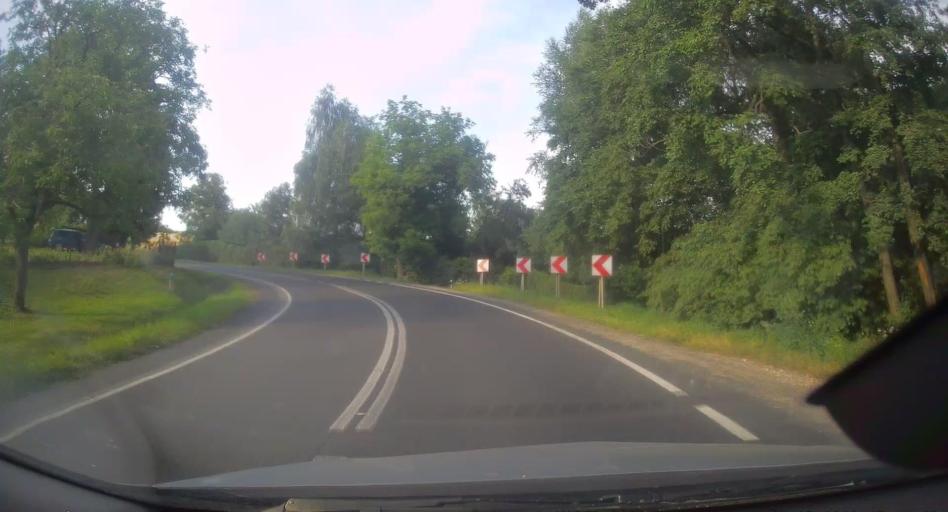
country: PL
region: Lesser Poland Voivodeship
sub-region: Powiat bochenski
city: Dziewin
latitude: 50.1498
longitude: 20.5192
